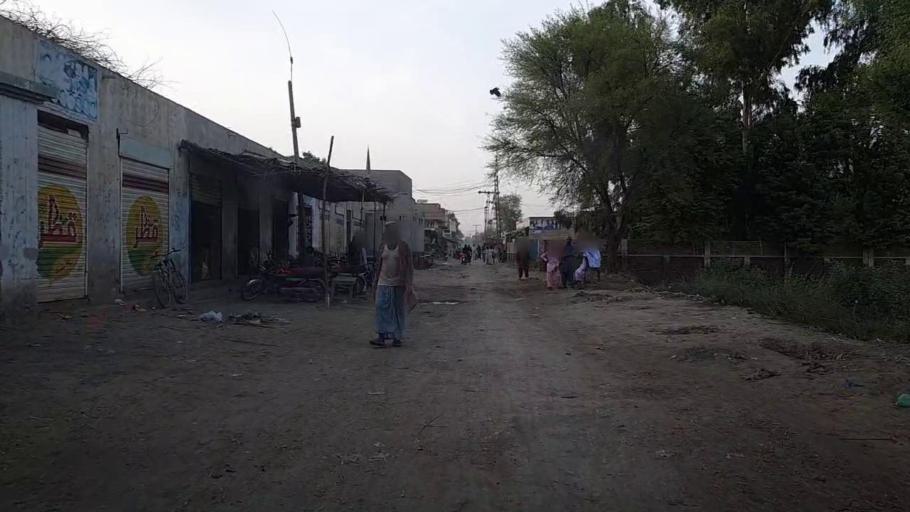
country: PK
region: Sindh
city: Ubauro
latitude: 28.2932
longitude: 69.7995
